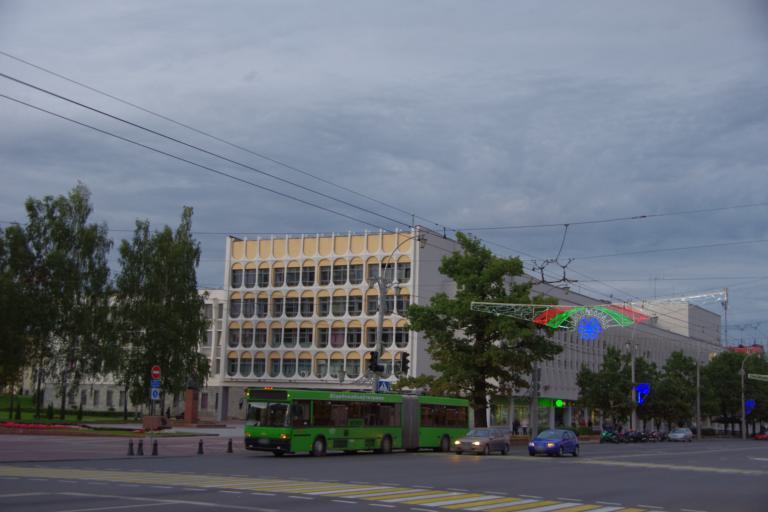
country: BY
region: Vitebsk
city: Vitebsk
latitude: 55.1923
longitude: 30.2065
